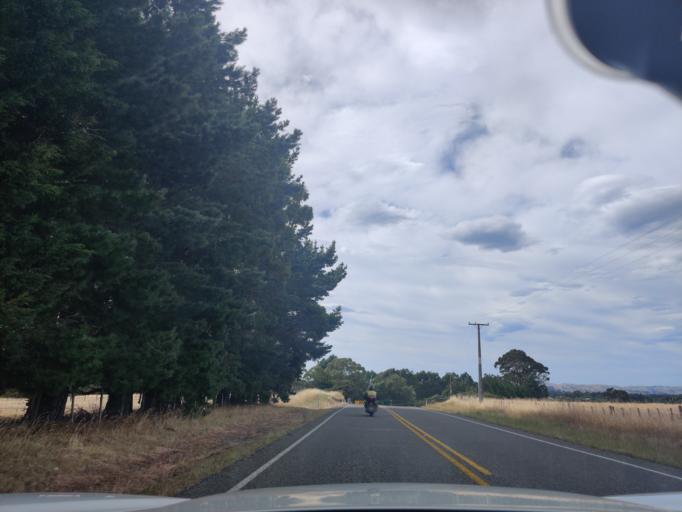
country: NZ
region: Wellington
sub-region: Masterton District
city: Masterton
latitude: -40.8803
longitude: 175.6569
